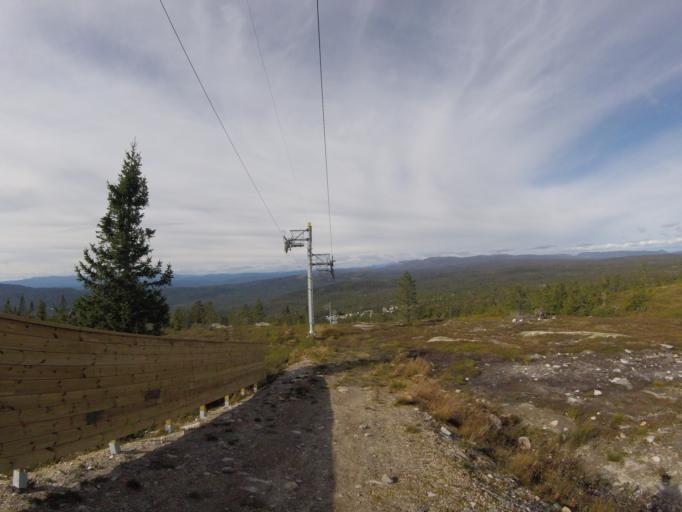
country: NO
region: Buskerud
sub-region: Flesberg
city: Lampeland
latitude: 59.7486
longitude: 9.4166
